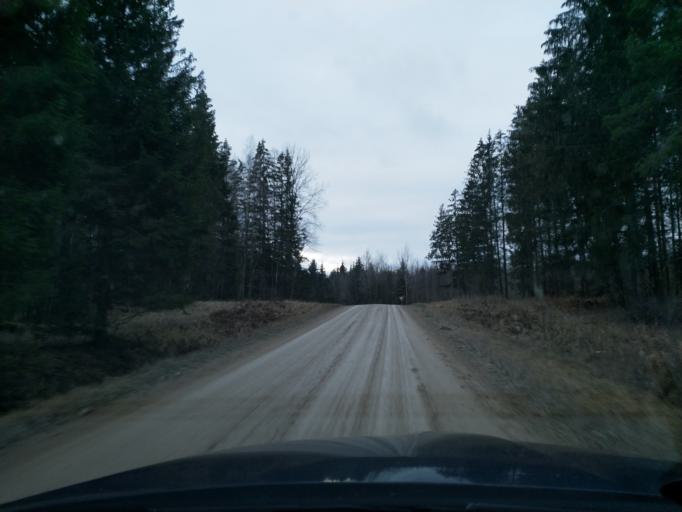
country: LV
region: Kuldigas Rajons
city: Kuldiga
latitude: 56.9013
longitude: 22.2563
